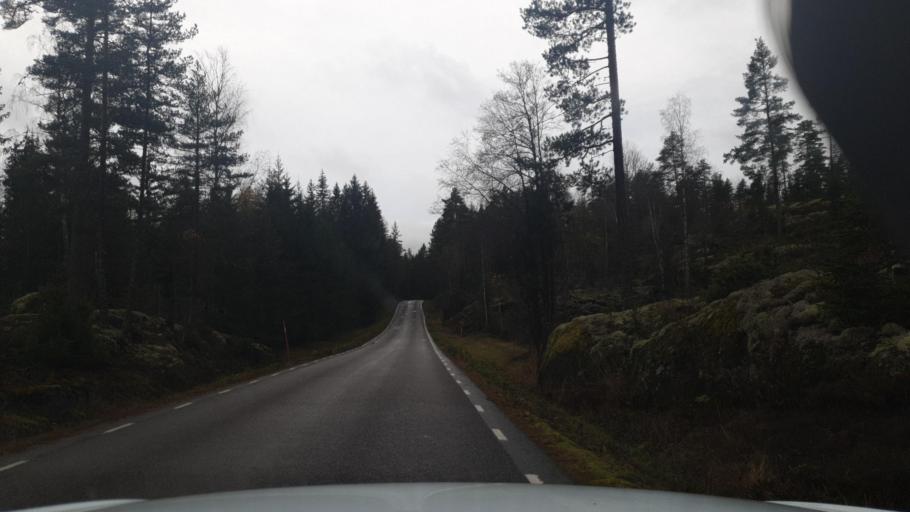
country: NO
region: Hedmark
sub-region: Eidskog
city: Skotterud
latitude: 59.8076
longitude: 12.0463
